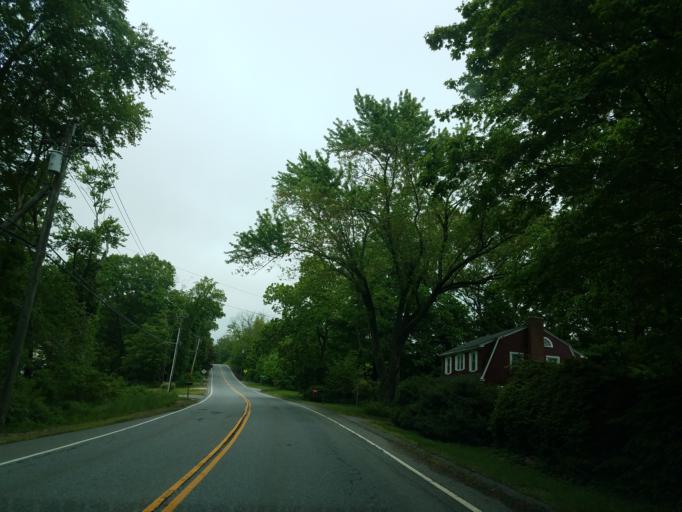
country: US
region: Connecticut
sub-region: New London County
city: Lisbon
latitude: 41.6132
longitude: -72.0161
